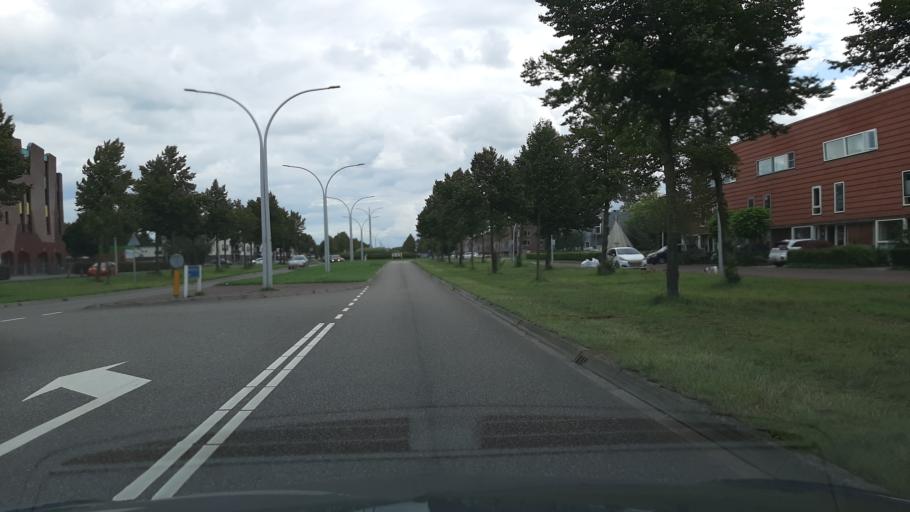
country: NL
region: Overijssel
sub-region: Gemeente Zwolle
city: Zwolle
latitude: 52.5393
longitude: 6.0577
